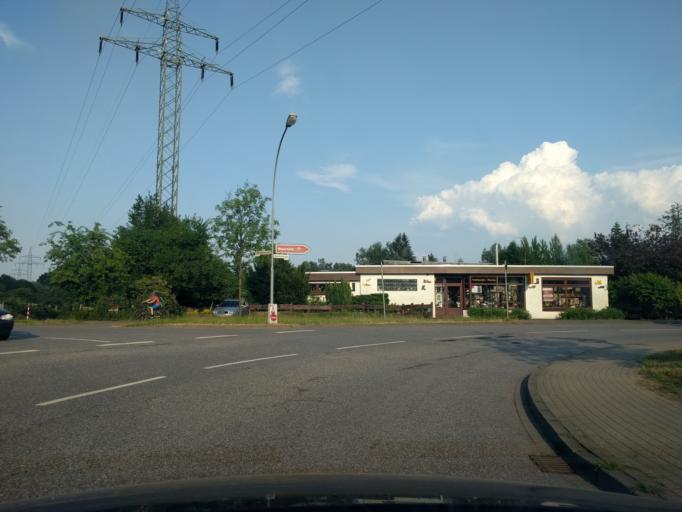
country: DE
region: Lower Saxony
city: Seevetal
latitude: 53.3886
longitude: 9.9827
